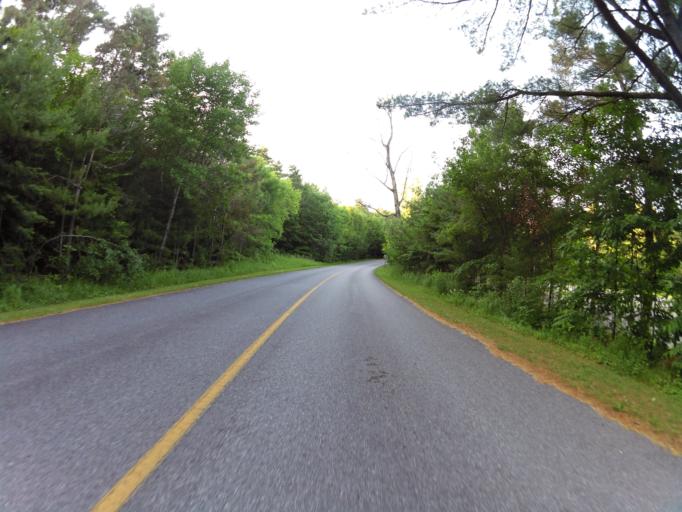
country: CA
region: Quebec
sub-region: Outaouais
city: Wakefield
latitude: 45.6140
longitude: -76.0110
